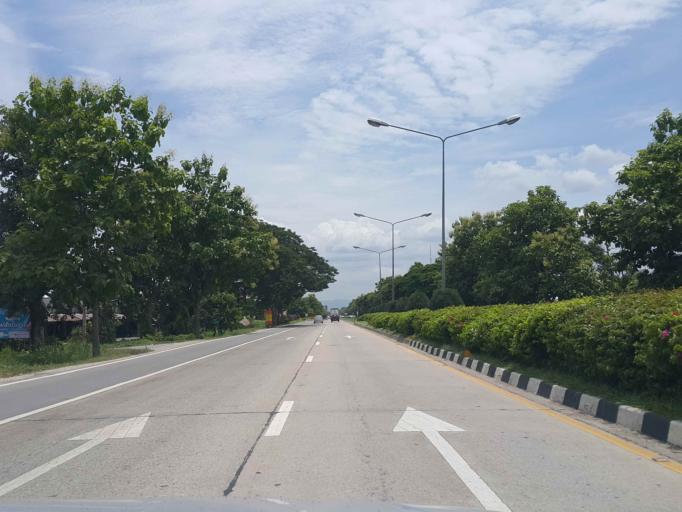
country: TH
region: Chiang Mai
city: Saraphi
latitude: 18.6612
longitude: 99.0522
